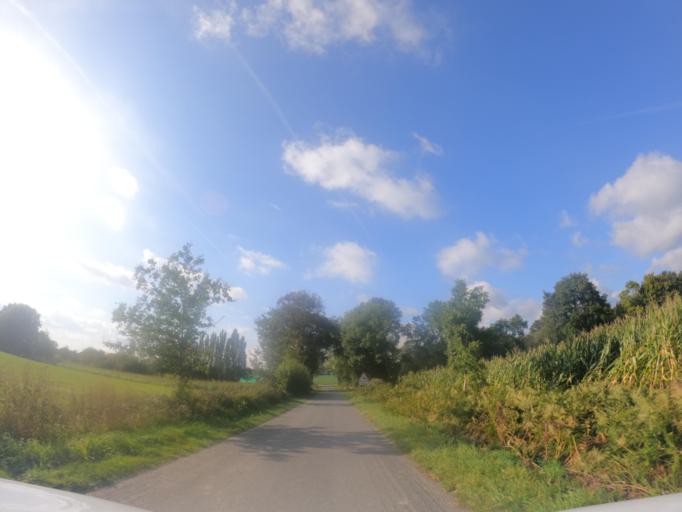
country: FR
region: Poitou-Charentes
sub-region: Departement des Deux-Sevres
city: Courlay
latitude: 46.7782
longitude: -0.6008
